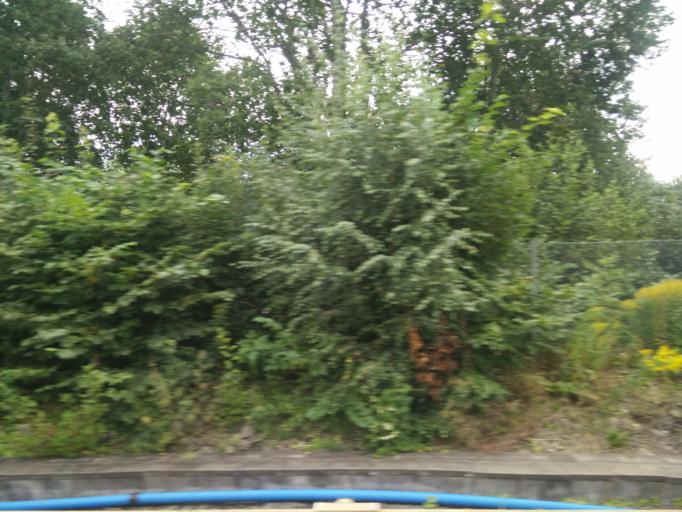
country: NO
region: Oslo
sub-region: Oslo
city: Sjolyststranda
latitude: 59.9429
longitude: 10.6733
